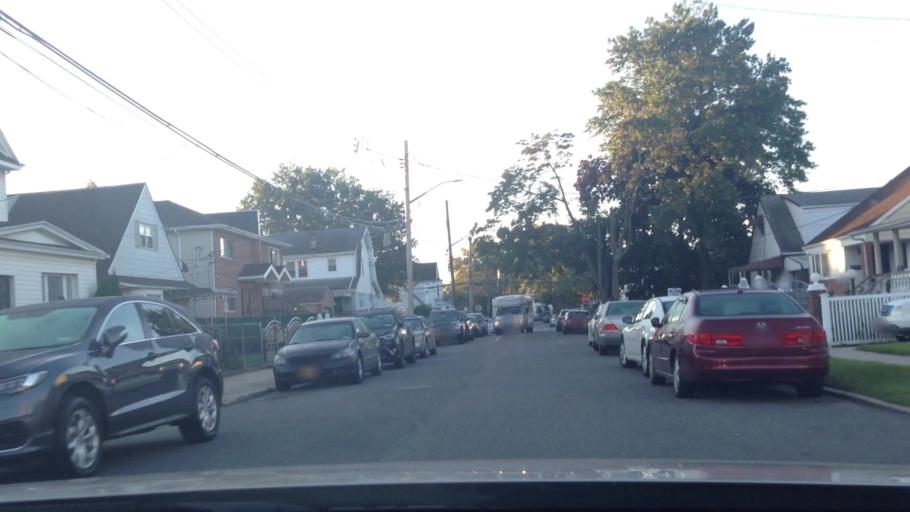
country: US
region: New York
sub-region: Queens County
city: Jamaica
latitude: 40.6712
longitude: -73.7784
